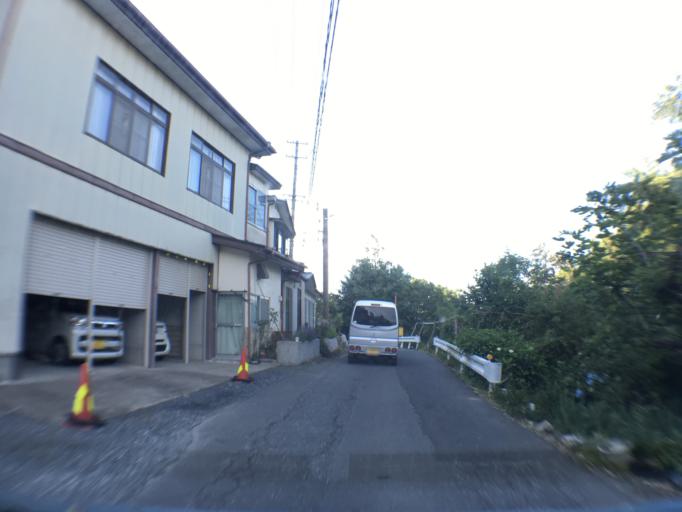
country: JP
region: Miyagi
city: Wakuya
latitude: 38.6467
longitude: 141.2817
